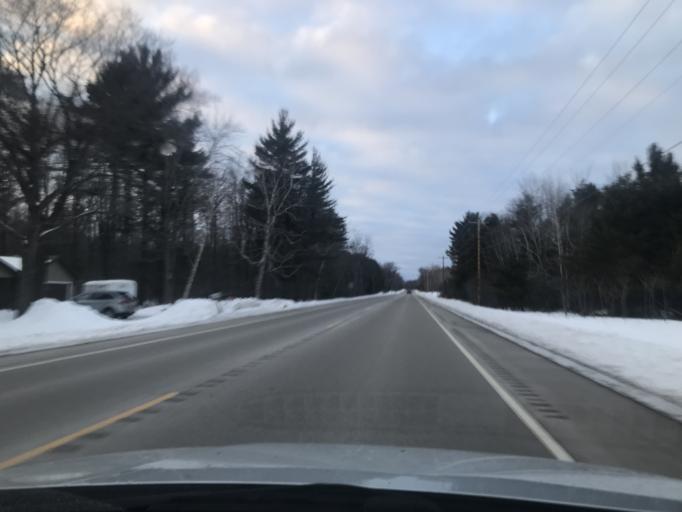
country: US
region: Wisconsin
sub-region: Marinette County
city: Marinette
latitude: 45.1468
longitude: -87.6995
